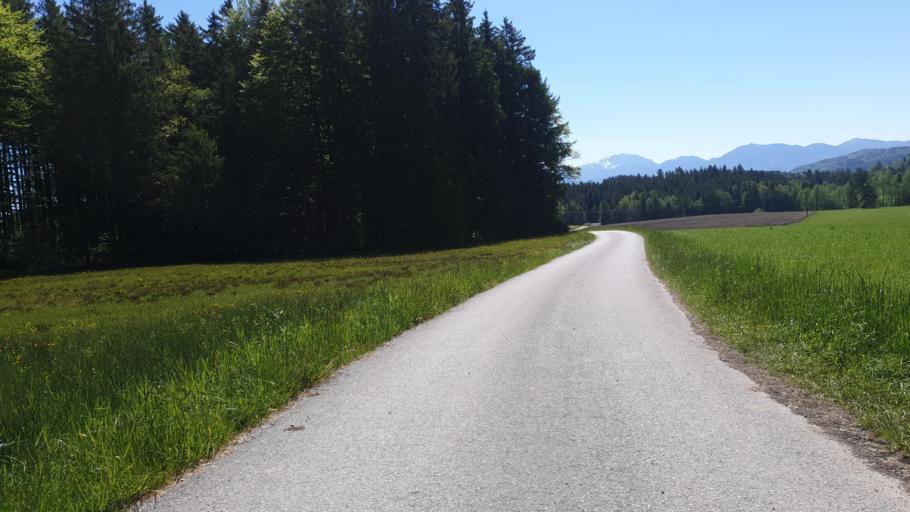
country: DE
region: Bavaria
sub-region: Upper Bavaria
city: Habach
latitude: 47.7557
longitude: 11.2612
